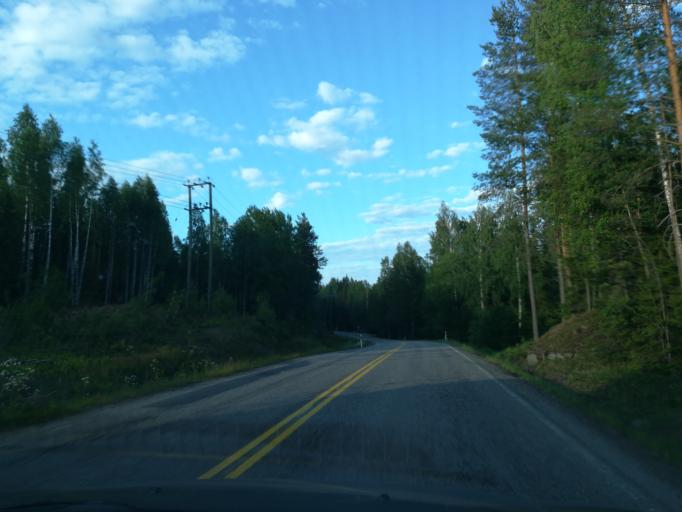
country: FI
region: Southern Savonia
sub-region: Mikkeli
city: Puumala
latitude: 61.5756
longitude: 28.1526
